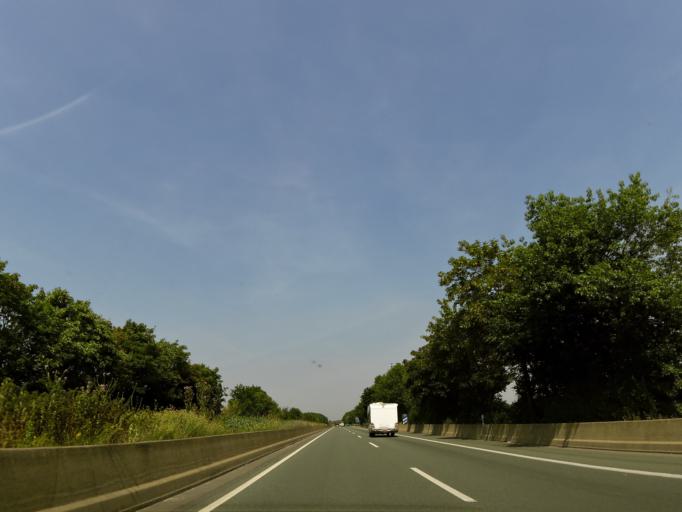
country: DE
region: North Rhine-Westphalia
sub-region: Regierungsbezirk Koln
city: Erftstadt
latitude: 50.8310
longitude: 6.7684
